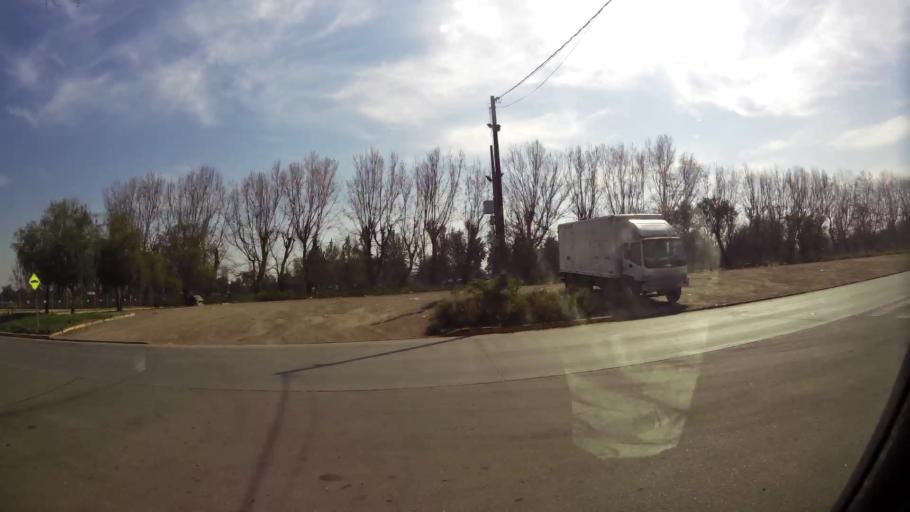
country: CL
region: Santiago Metropolitan
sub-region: Provincia de Santiago
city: Lo Prado
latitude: -33.4551
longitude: -70.7344
